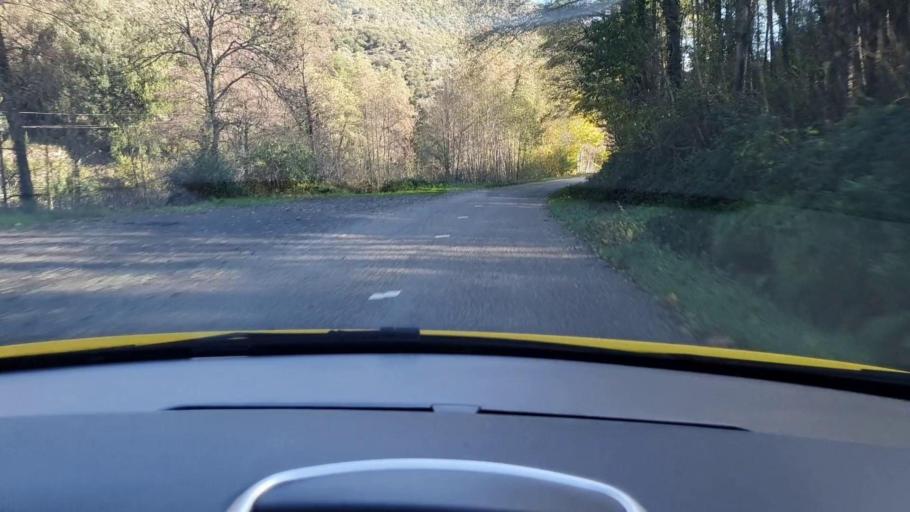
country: FR
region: Languedoc-Roussillon
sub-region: Departement du Gard
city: Valleraugue
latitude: 44.1691
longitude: 3.6516
